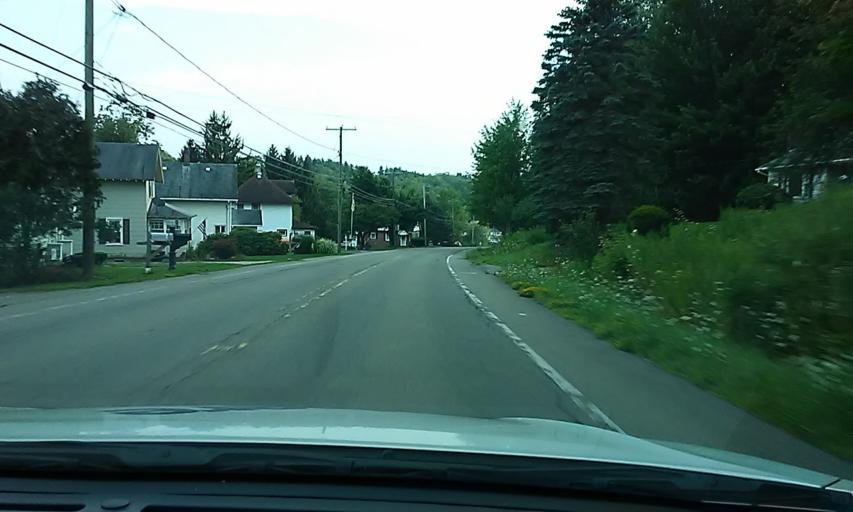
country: US
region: Pennsylvania
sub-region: McKean County
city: Kane
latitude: 41.6414
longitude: -78.8144
